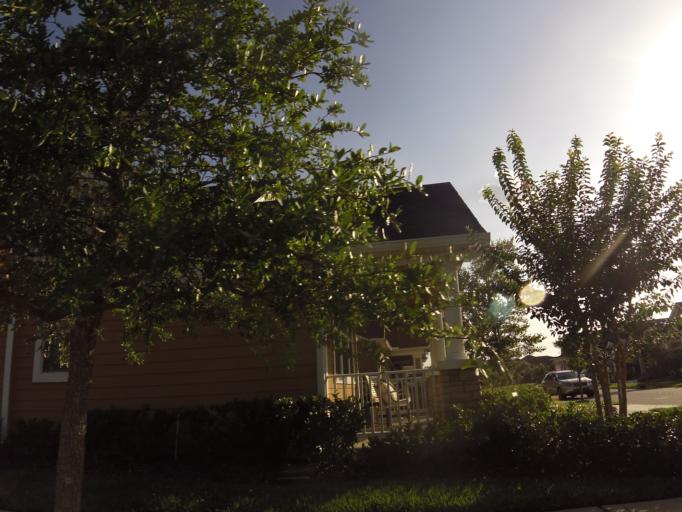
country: US
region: Florida
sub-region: Clay County
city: Green Cove Springs
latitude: 30.0258
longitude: -81.6356
